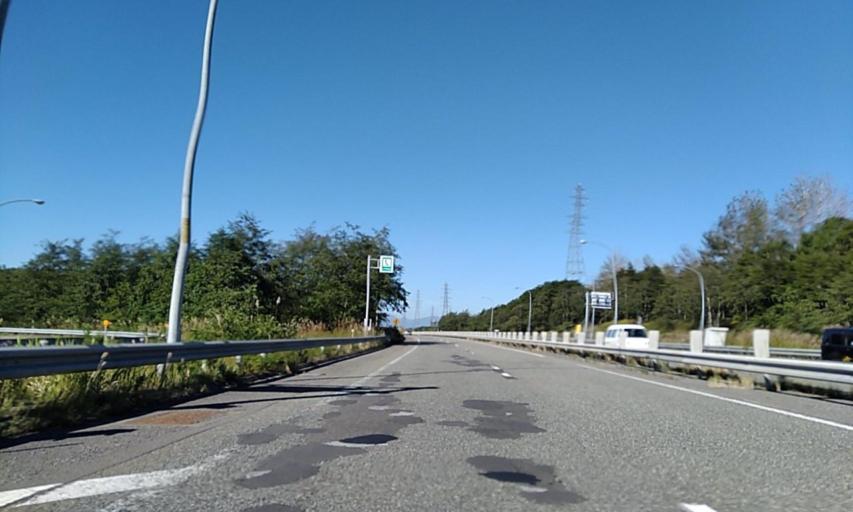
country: JP
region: Hokkaido
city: Tomakomai
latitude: 42.6728
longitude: 141.7829
